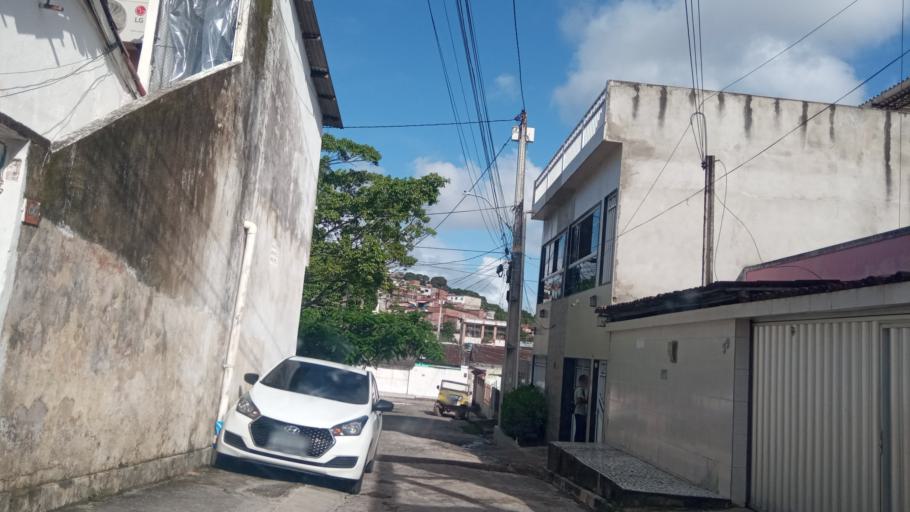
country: BR
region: Pernambuco
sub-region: Jaboatao Dos Guararapes
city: Jaboatao dos Guararapes
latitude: -8.1326
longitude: -34.9501
